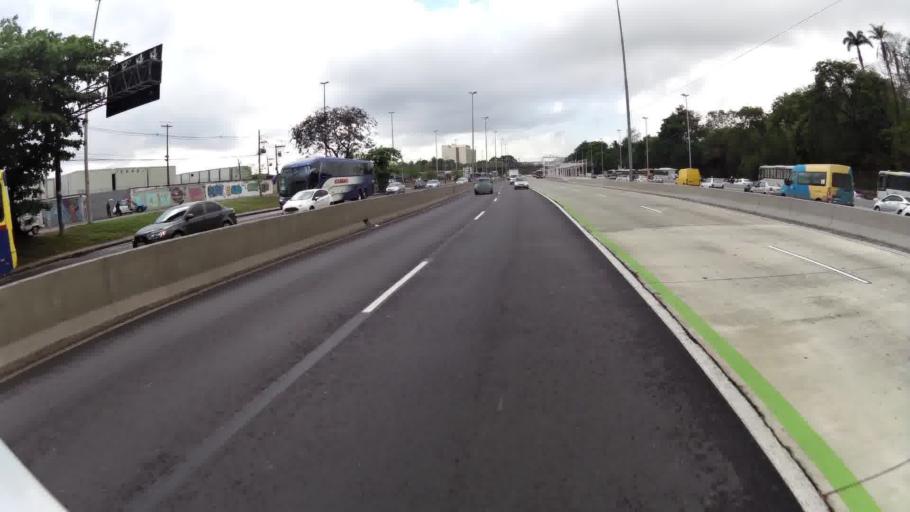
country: BR
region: Rio de Janeiro
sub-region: Rio De Janeiro
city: Rio de Janeiro
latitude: -22.8737
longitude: -43.2440
